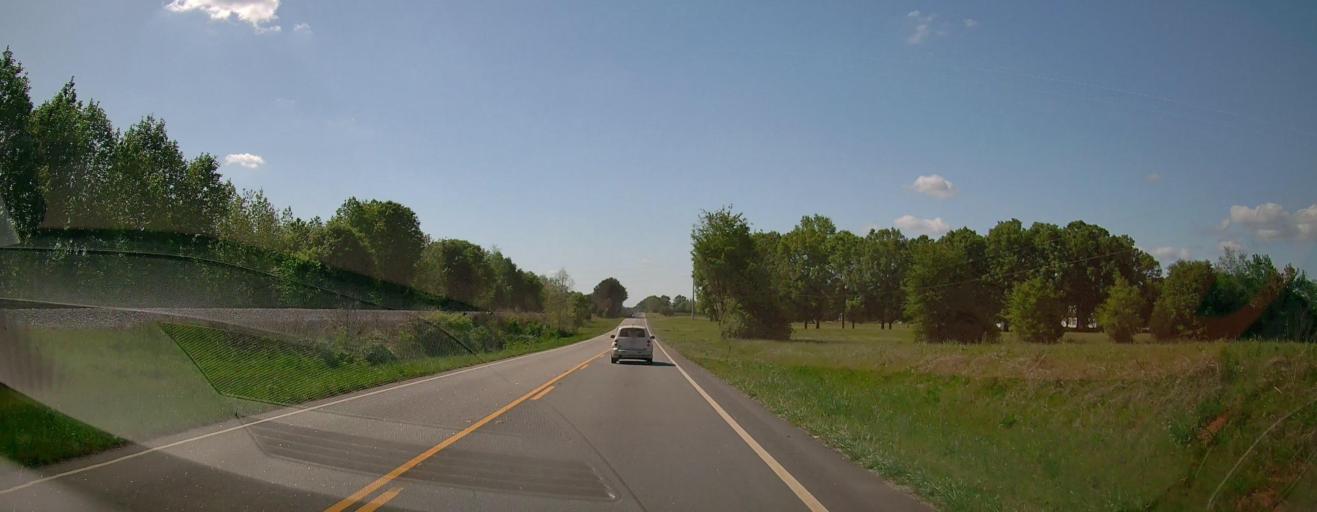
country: US
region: Georgia
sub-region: Morgan County
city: Madison
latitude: 33.6032
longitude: -83.4249
